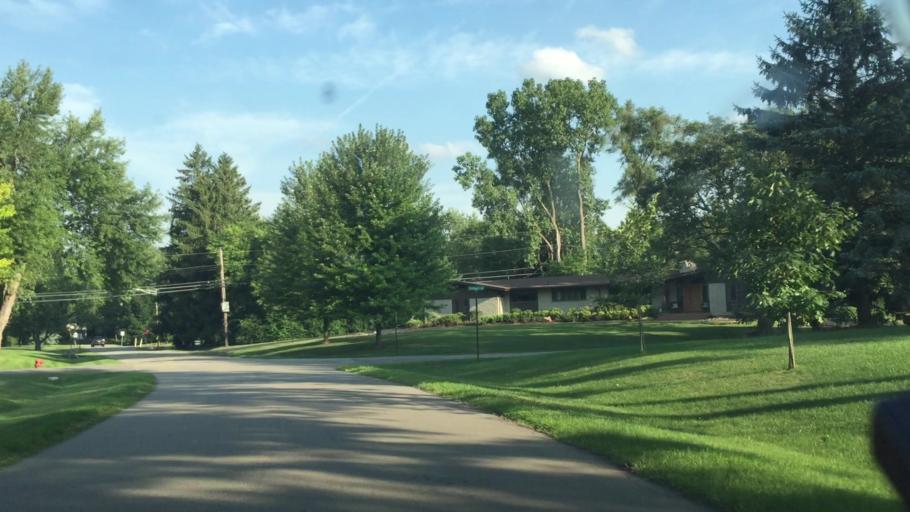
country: US
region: Michigan
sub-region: Oakland County
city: Bloomfield Hills
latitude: 42.5565
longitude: -83.2714
